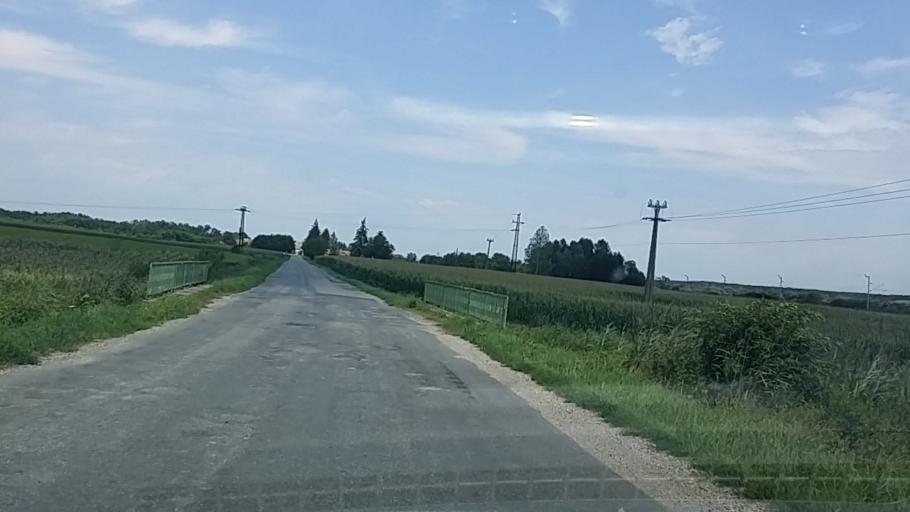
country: HU
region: Zala
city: Murakeresztur
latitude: 46.3681
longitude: 16.8950
